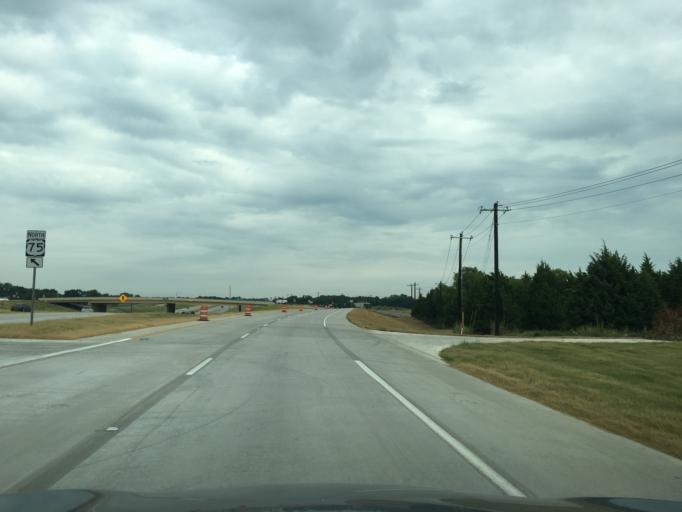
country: US
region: Texas
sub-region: Collin County
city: Melissa
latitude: 33.3160
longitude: -96.5902
